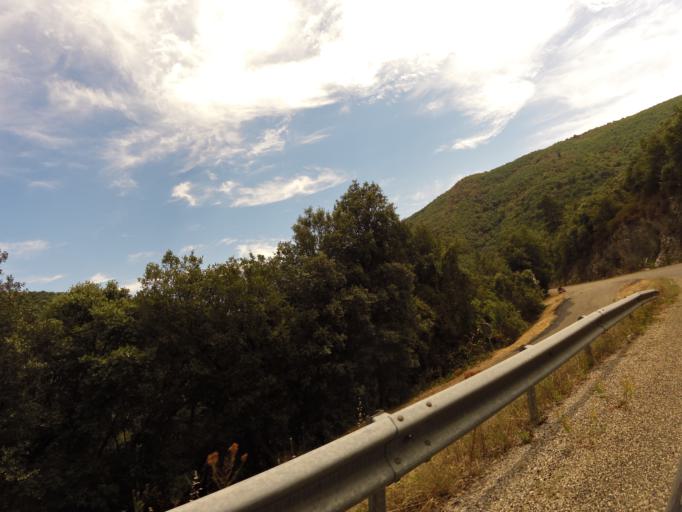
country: FR
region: Languedoc-Roussillon
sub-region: Departement du Gard
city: Le Vigan
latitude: 44.0037
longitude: 3.6575
